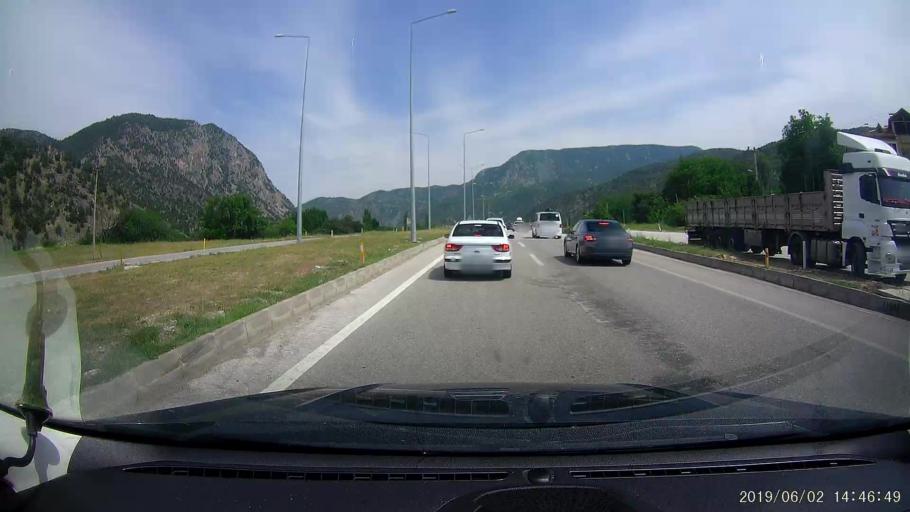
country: TR
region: Corum
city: Hacihamza
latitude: 41.0734
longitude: 34.4551
